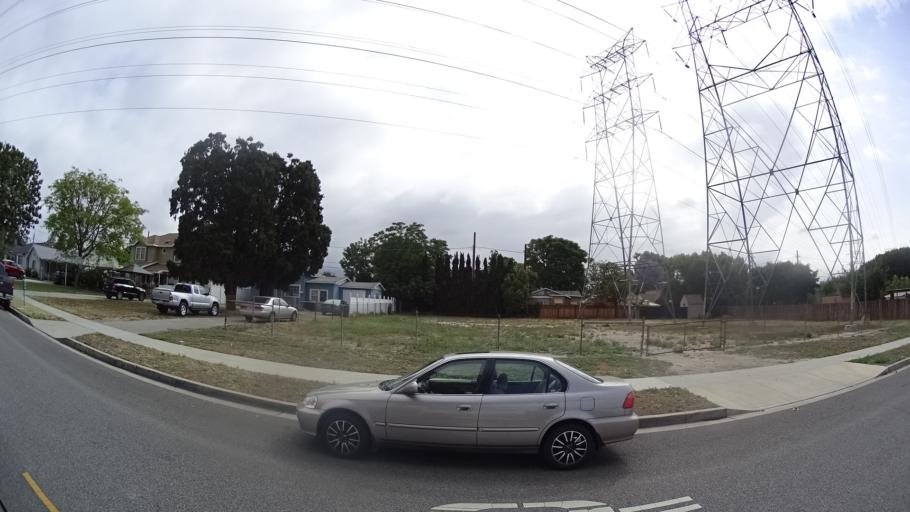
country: US
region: California
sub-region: Los Angeles County
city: North Hollywood
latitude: 34.1688
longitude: -118.3521
